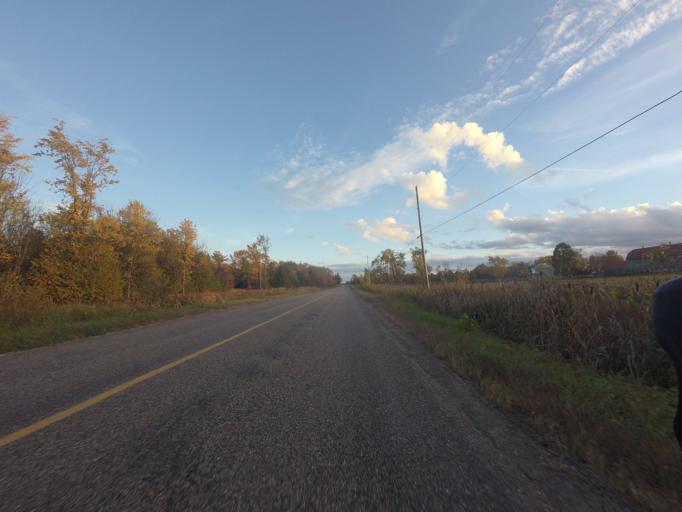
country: CA
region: Ontario
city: Renfrew
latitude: 45.4438
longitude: -76.9664
